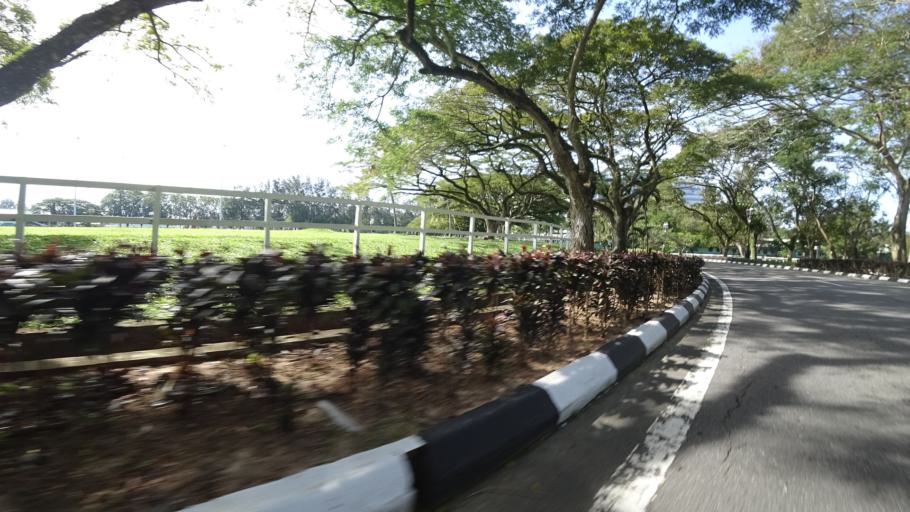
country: BN
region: Brunei and Muara
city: Bandar Seri Begawan
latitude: 4.9470
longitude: 114.8333
